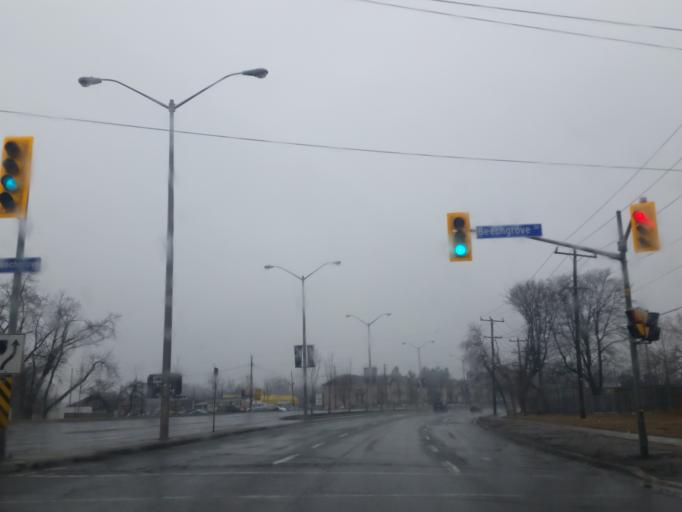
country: CA
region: Ontario
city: Scarborough
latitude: 43.7765
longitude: -79.1737
